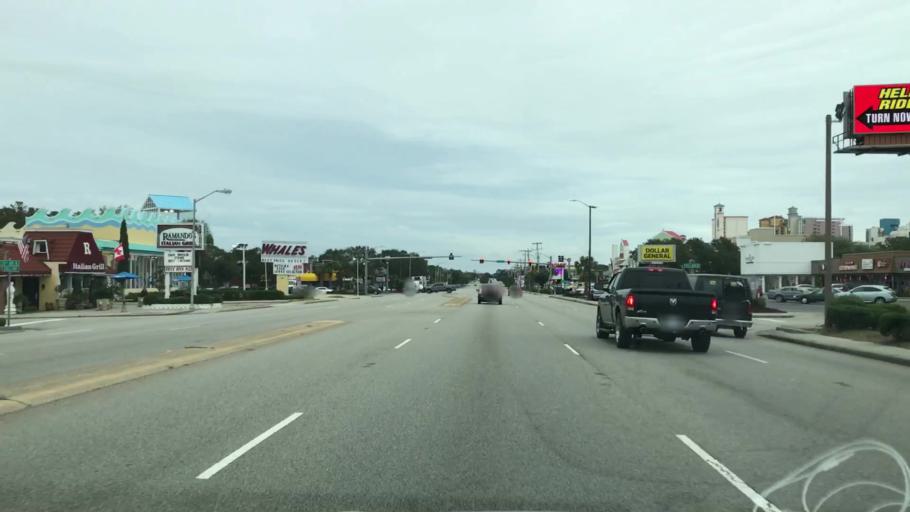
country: US
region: South Carolina
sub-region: Horry County
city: Myrtle Beach
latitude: 33.7013
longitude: -78.8731
